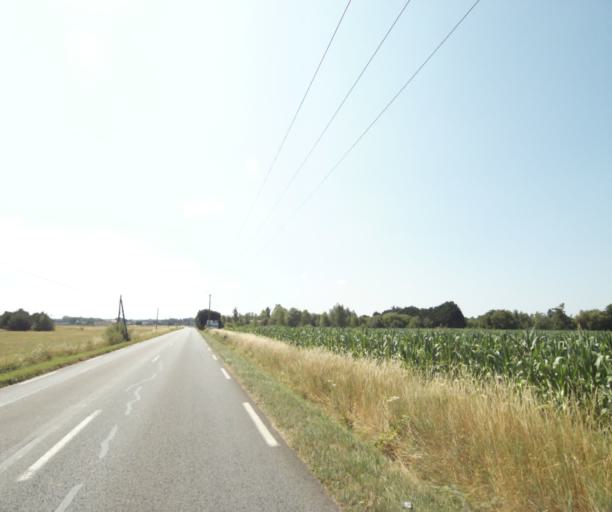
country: FR
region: Centre
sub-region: Departement du Loiret
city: Saint-Cyr-en-Val
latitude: 47.8413
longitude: 1.9615
